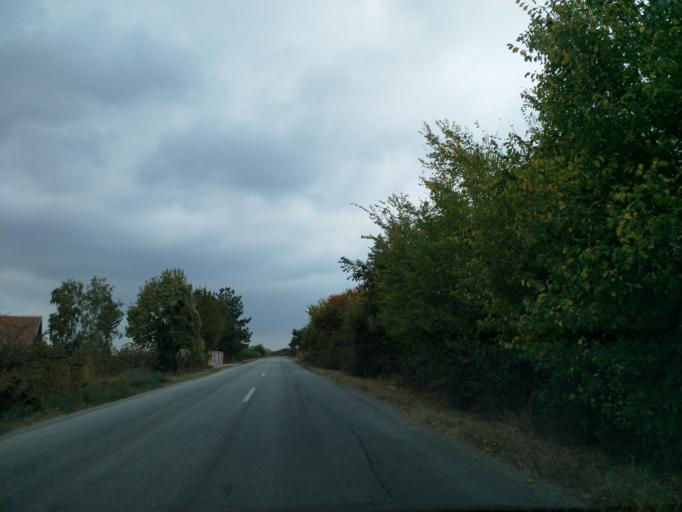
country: RS
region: Central Serbia
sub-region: Pomoravski Okrug
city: Jagodina
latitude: 44.0097
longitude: 21.2020
